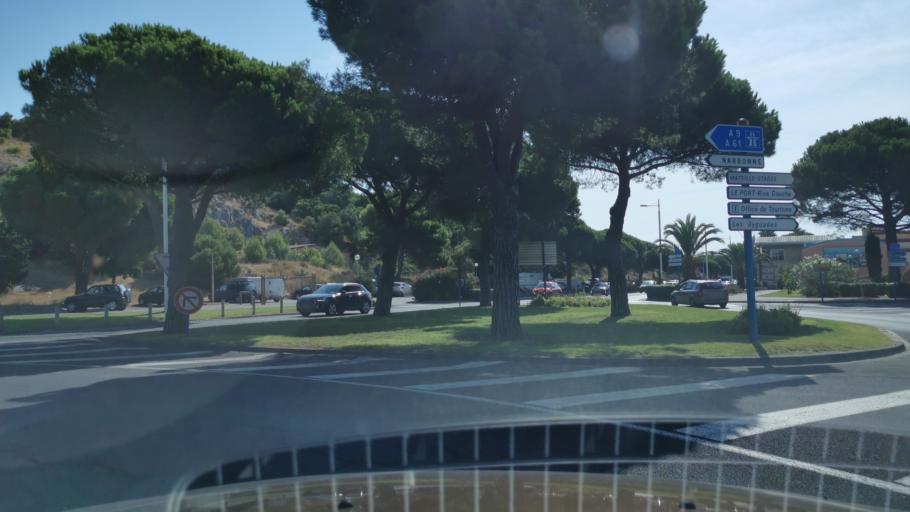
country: FR
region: Languedoc-Roussillon
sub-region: Departement de l'Aude
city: Gruissan
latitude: 43.1118
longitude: 3.0941
